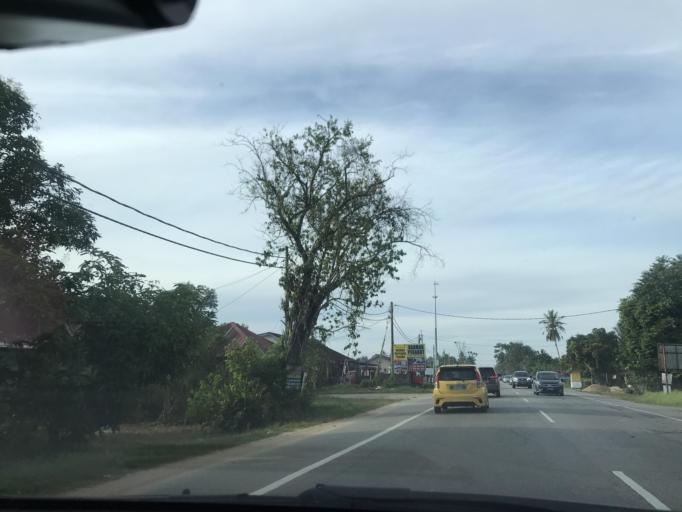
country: MY
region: Kelantan
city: Kampong Kadok
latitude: 5.9822
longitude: 102.1898
